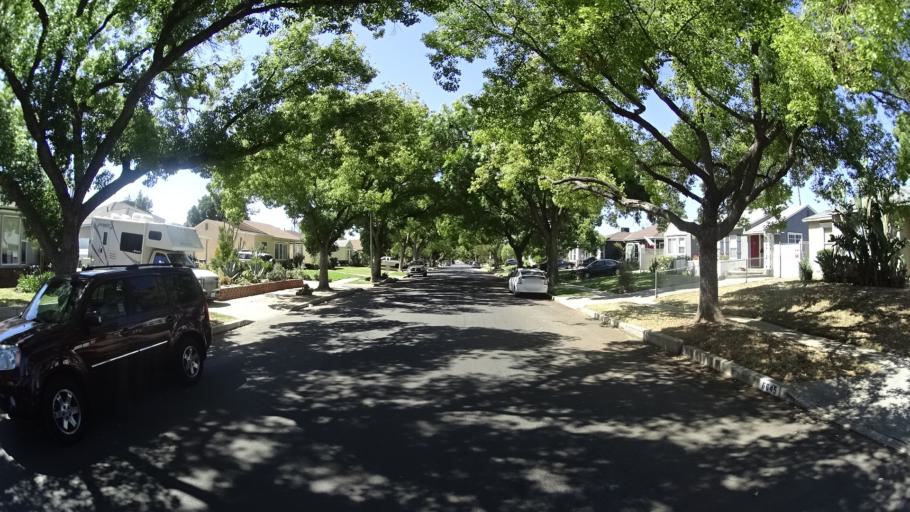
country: US
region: California
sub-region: Los Angeles County
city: Van Nuys
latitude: 34.1917
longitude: -118.4991
